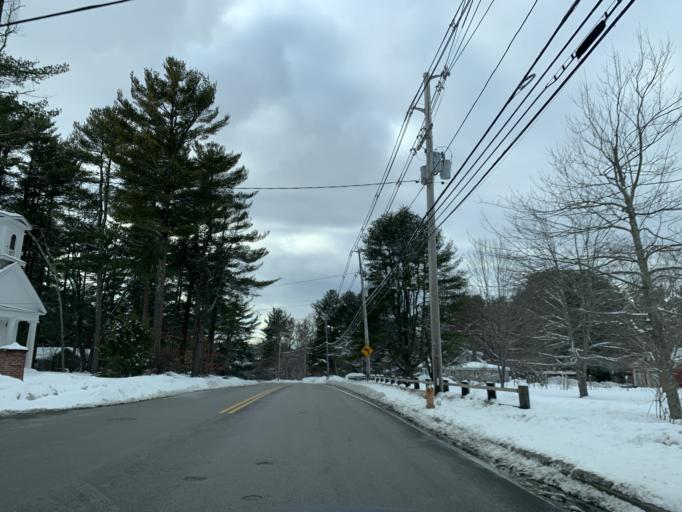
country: US
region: Massachusetts
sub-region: Norfolk County
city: Franklin
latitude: 42.0561
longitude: -71.4295
